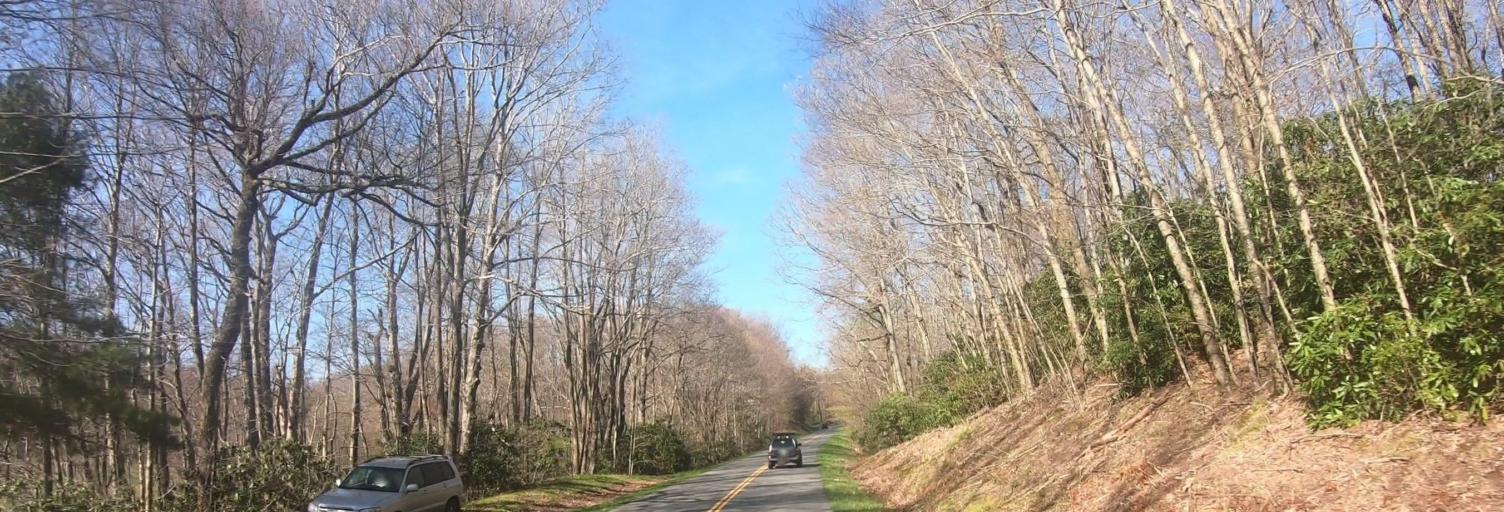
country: US
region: North Carolina
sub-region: Watauga County
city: Boone
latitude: 36.2033
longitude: -81.6040
